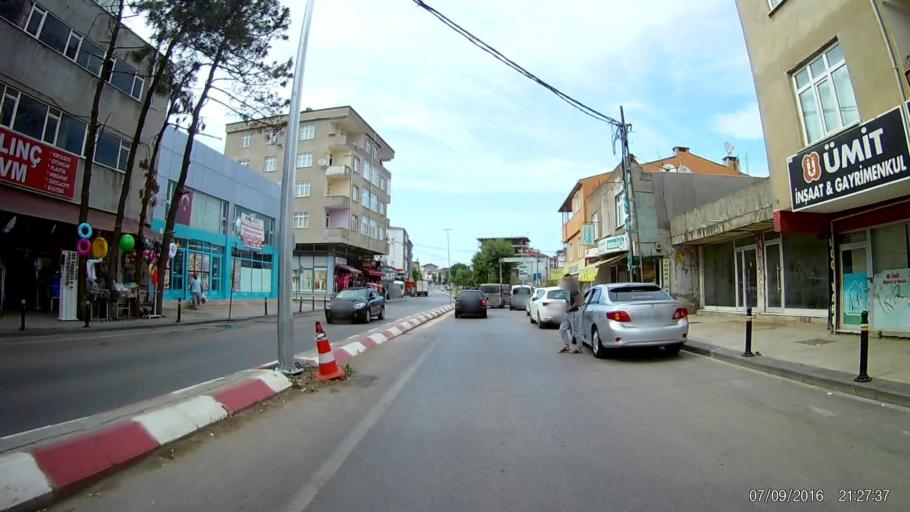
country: TR
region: Istanbul
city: Sultanbeyli
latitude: 40.9870
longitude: 29.2641
